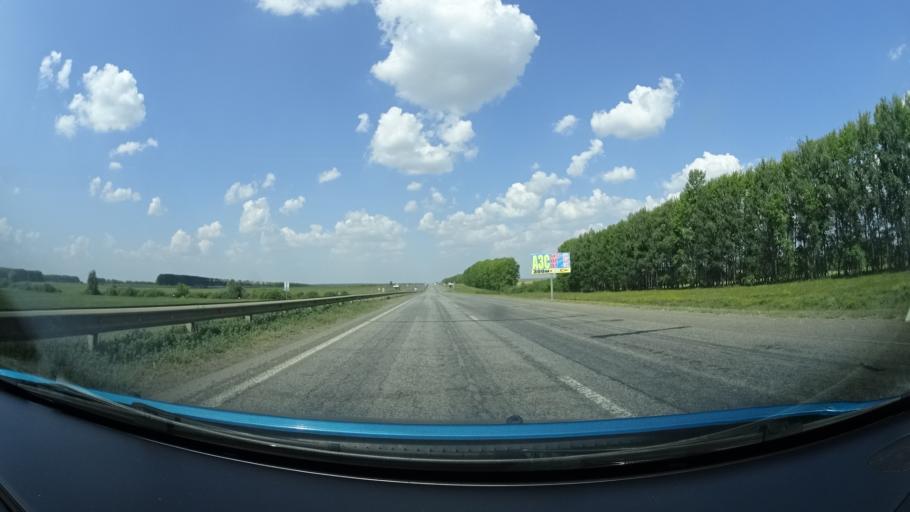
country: RU
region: Bashkortostan
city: Alekseyevka
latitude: 54.7200
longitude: 55.1811
